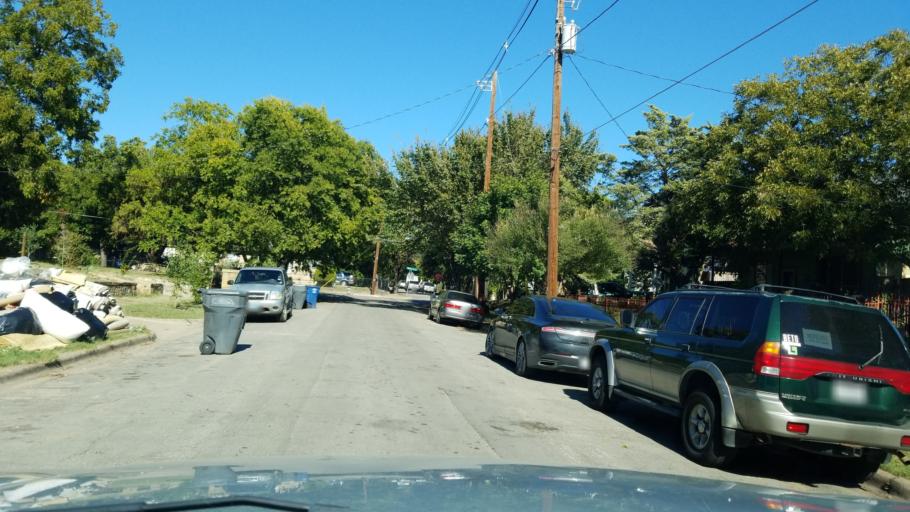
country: US
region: Texas
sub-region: Dallas County
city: Dallas
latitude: 32.7926
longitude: -96.7538
